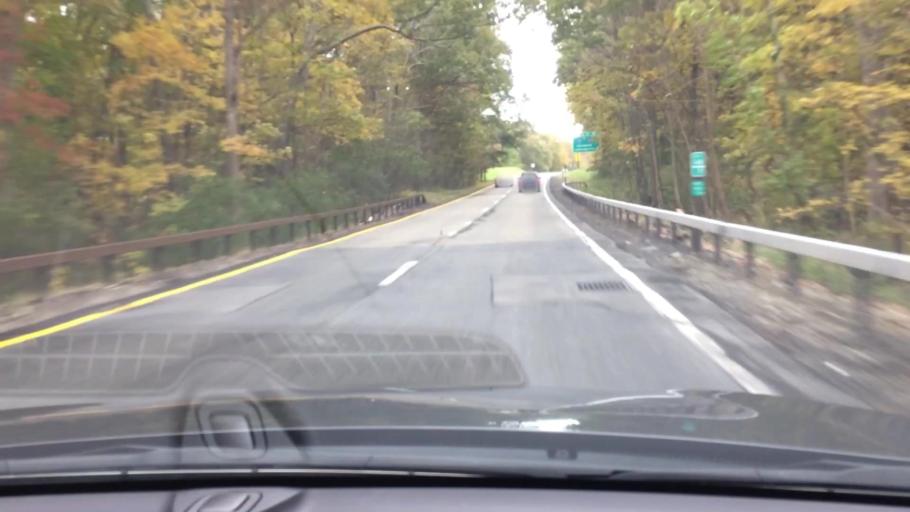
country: US
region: New York
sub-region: Dutchess County
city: Hillside Lake
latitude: 41.6366
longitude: -73.7834
